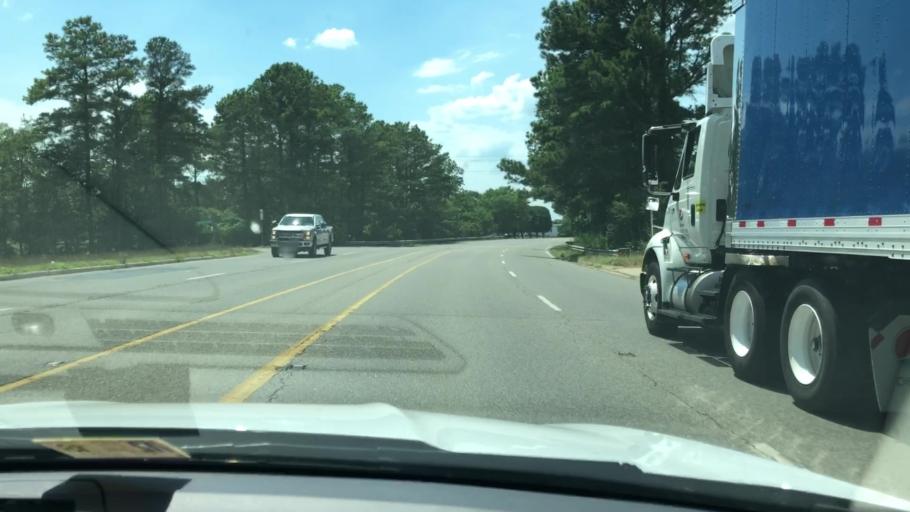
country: US
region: Virginia
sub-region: King William County
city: West Point
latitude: 37.5342
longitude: -76.7755
